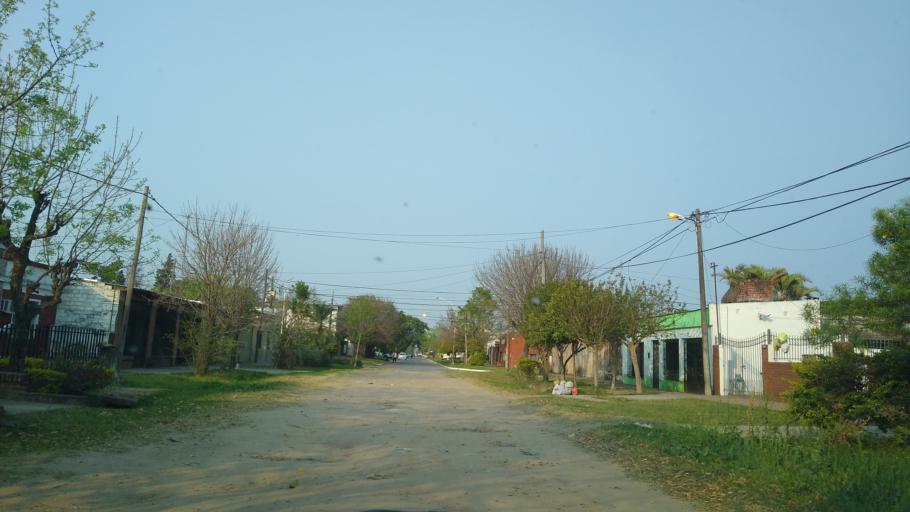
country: AR
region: Chaco
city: Barranqueras
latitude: -27.4812
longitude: -58.9430
